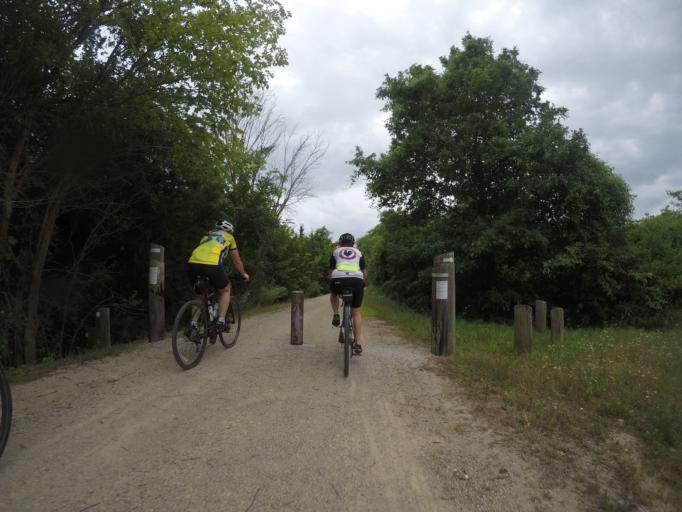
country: US
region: Kansas
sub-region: Anderson County
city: Garnett
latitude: 38.2414
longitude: -95.2576
